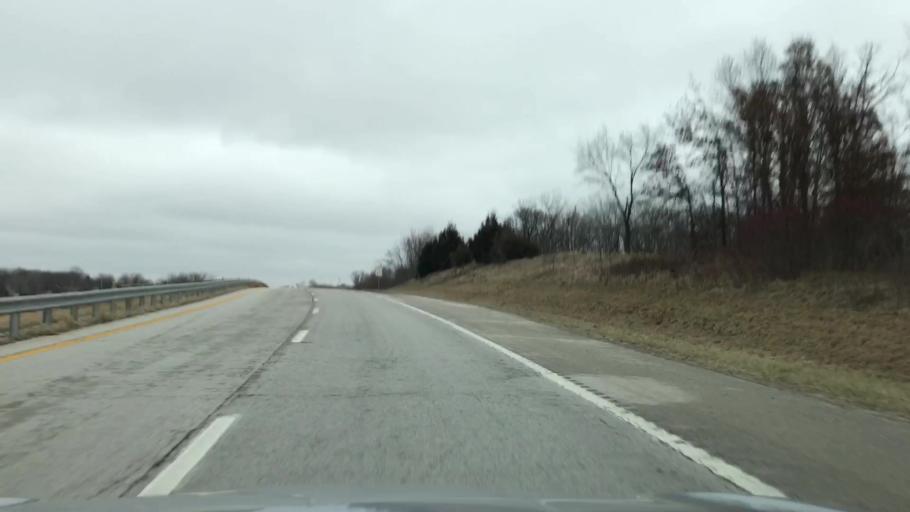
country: US
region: Missouri
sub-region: Linn County
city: Marceline
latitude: 39.7603
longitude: -92.9278
